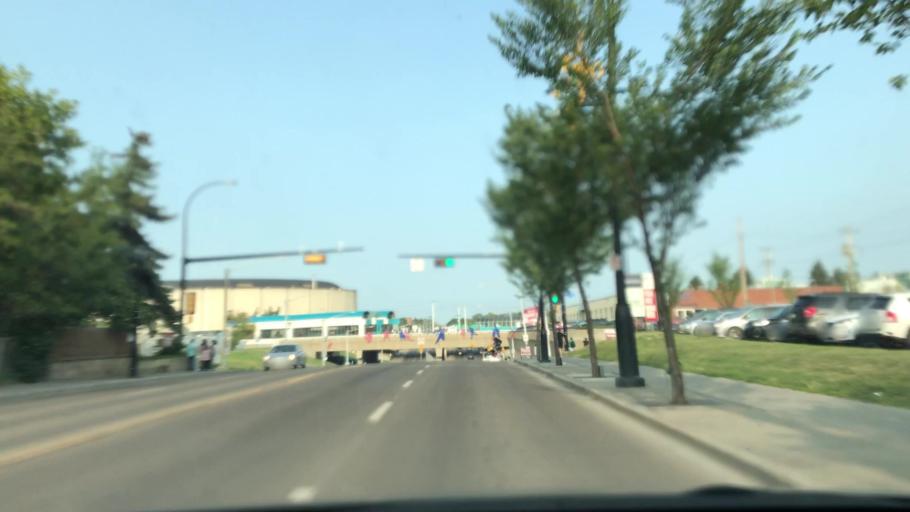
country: CA
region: Alberta
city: Edmonton
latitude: 53.5704
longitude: -113.4620
